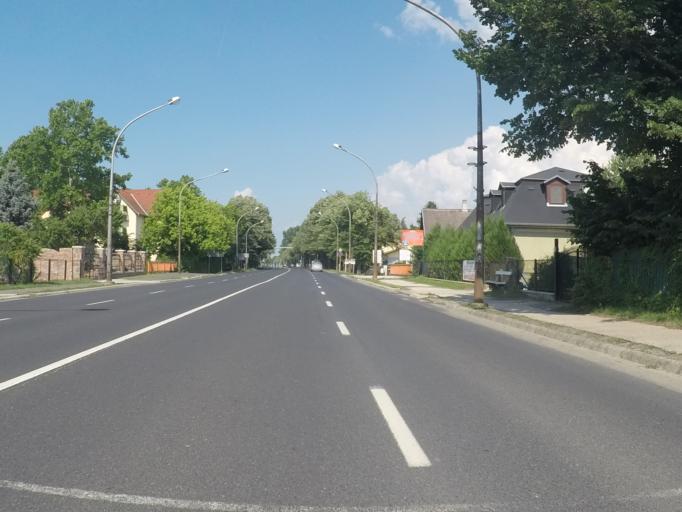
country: HU
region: Somogy
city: Balatonfoldvar
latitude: 46.8504
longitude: 17.8815
